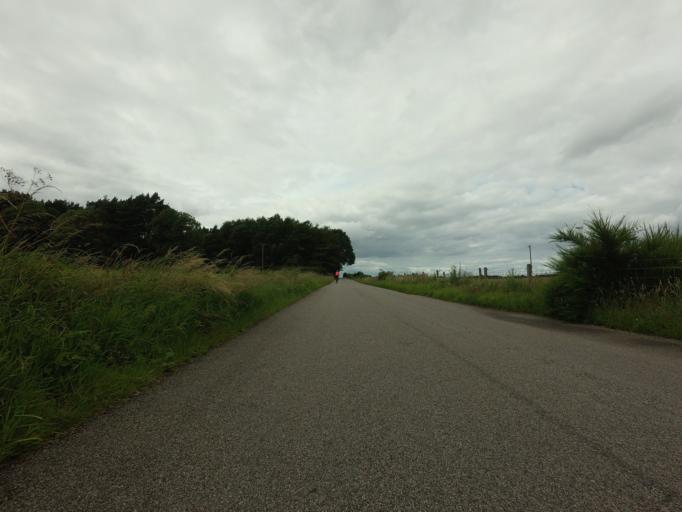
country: GB
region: Scotland
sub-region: Moray
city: Forres
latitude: 57.6017
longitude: -3.7238
